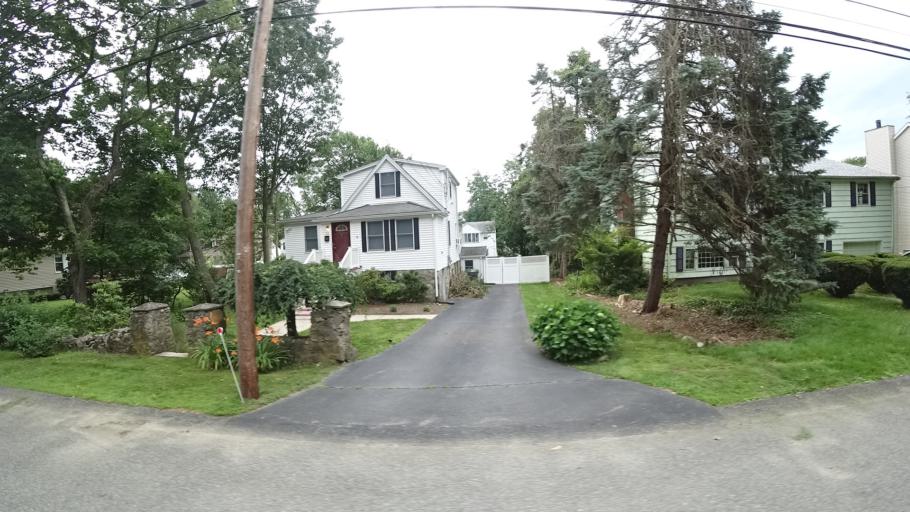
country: US
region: Massachusetts
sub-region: Norfolk County
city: Dedham
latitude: 42.2276
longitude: -71.1480
